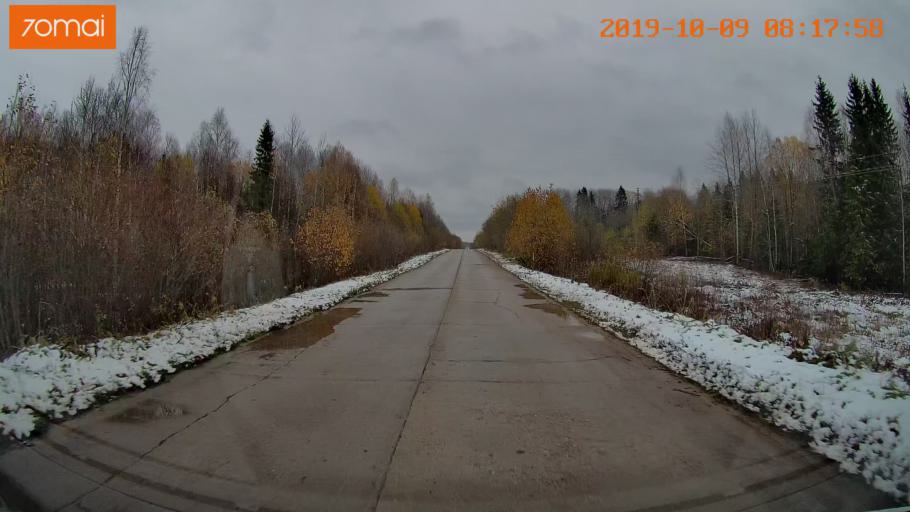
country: RU
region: Vologda
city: Gryazovets
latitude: 58.7395
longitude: 40.2150
